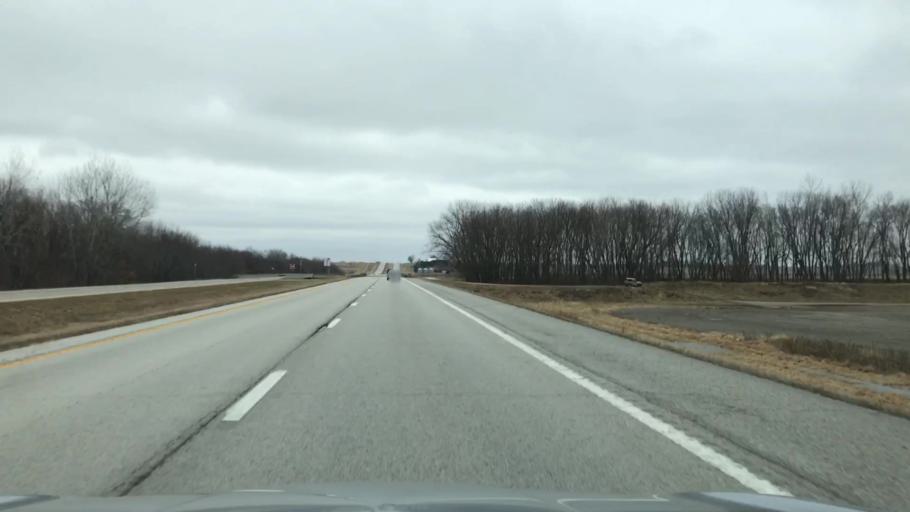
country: US
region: Missouri
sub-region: Livingston County
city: Chillicothe
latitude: 39.7768
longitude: -93.4179
